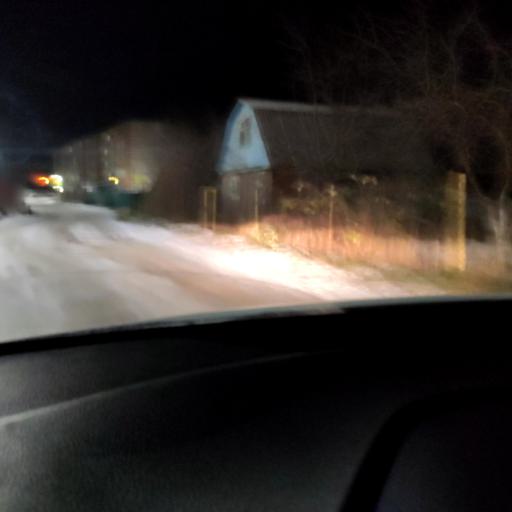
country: RU
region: Tatarstan
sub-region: Gorod Kazan'
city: Kazan
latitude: 55.7178
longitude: 49.0940
